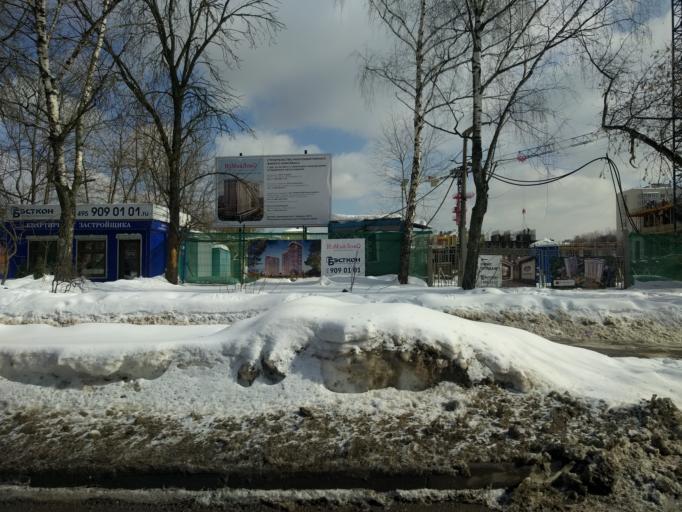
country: RU
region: Moscow
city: Metrogorodok
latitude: 55.7998
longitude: 37.7751
